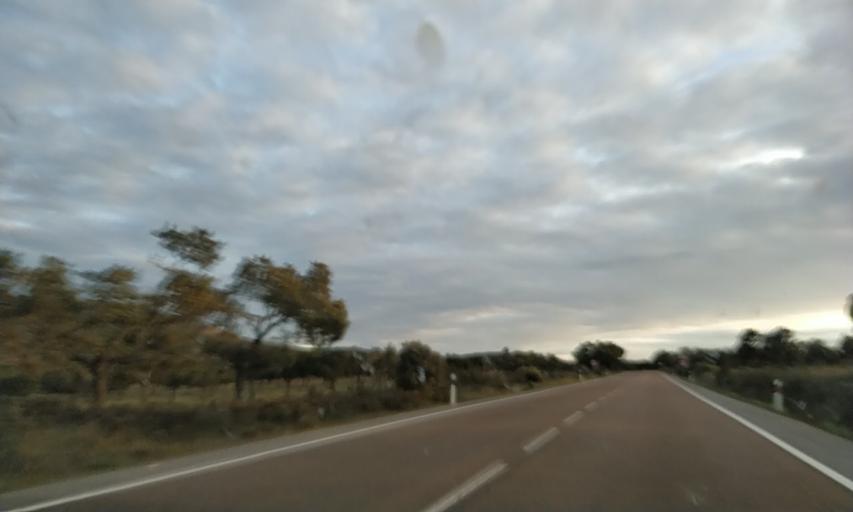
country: ES
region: Extremadura
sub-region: Provincia de Badajoz
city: Puebla de Obando
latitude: 39.2109
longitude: -6.5844
